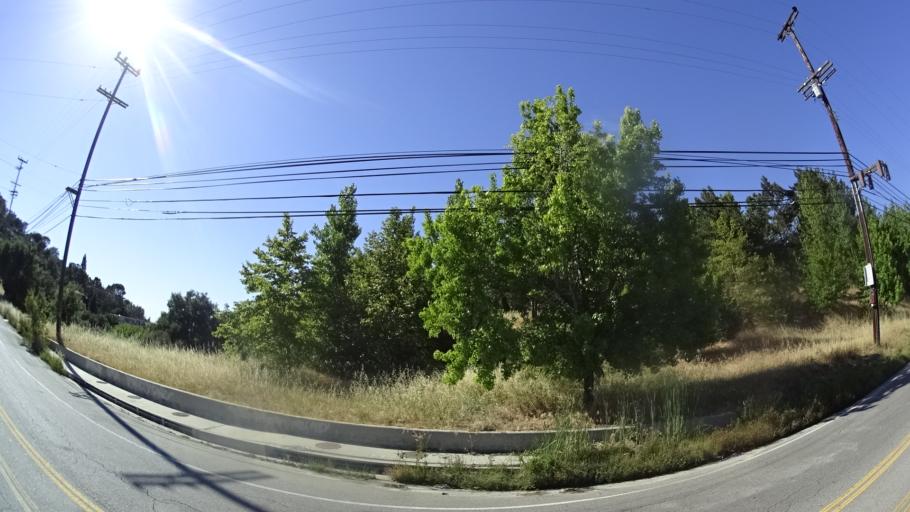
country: US
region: California
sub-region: Los Angeles County
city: Sherman Oaks
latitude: 34.1306
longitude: -118.4590
